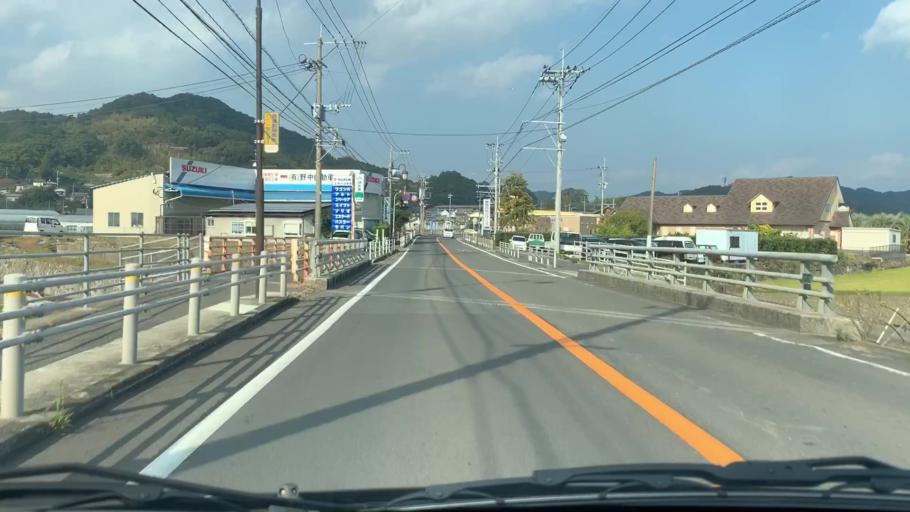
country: JP
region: Nagasaki
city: Togitsu
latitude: 32.9437
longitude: 129.7821
